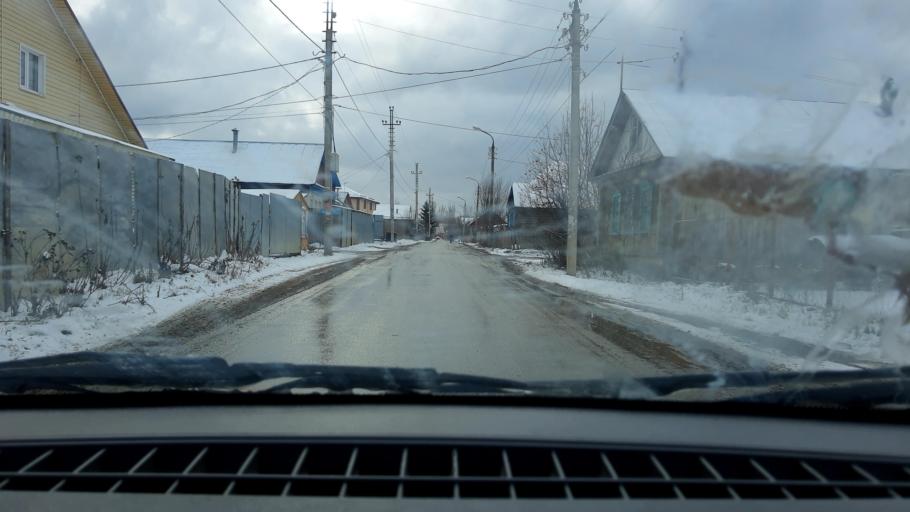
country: RU
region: Bashkortostan
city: Ufa
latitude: 54.7064
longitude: 55.9475
